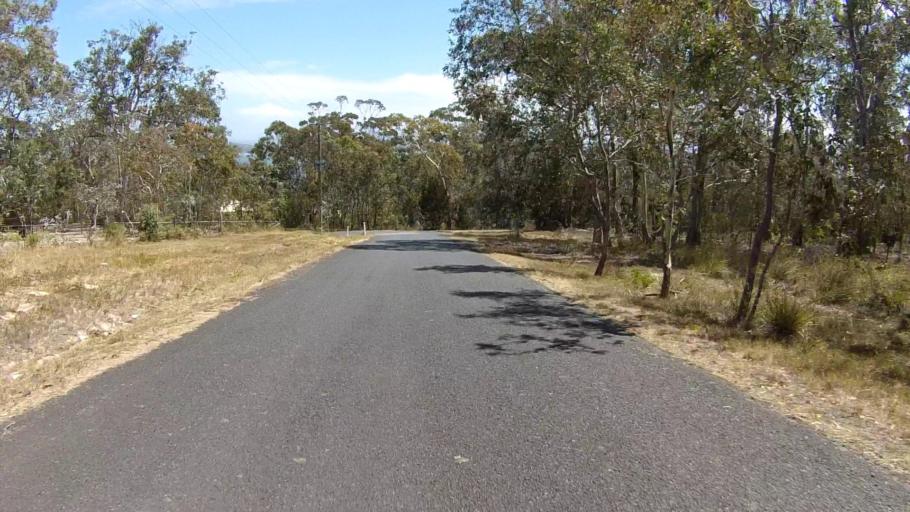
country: AU
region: Tasmania
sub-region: Clarence
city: Sandford
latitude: -43.0075
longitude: 147.4777
